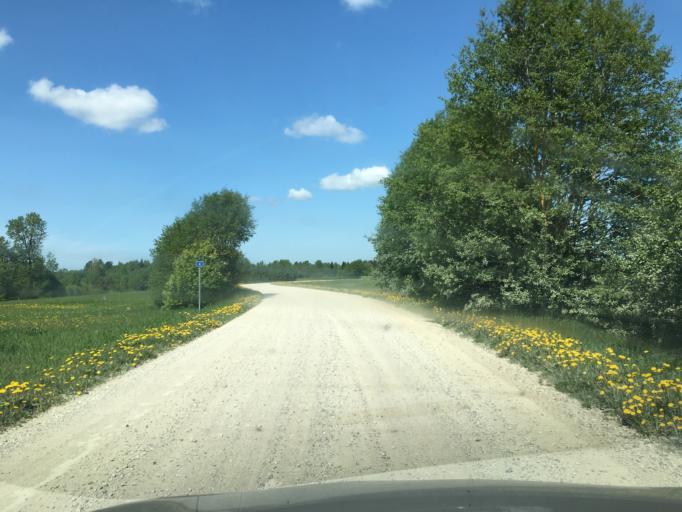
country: EE
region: Harju
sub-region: Saue linn
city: Saue
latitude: 59.2879
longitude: 24.5074
